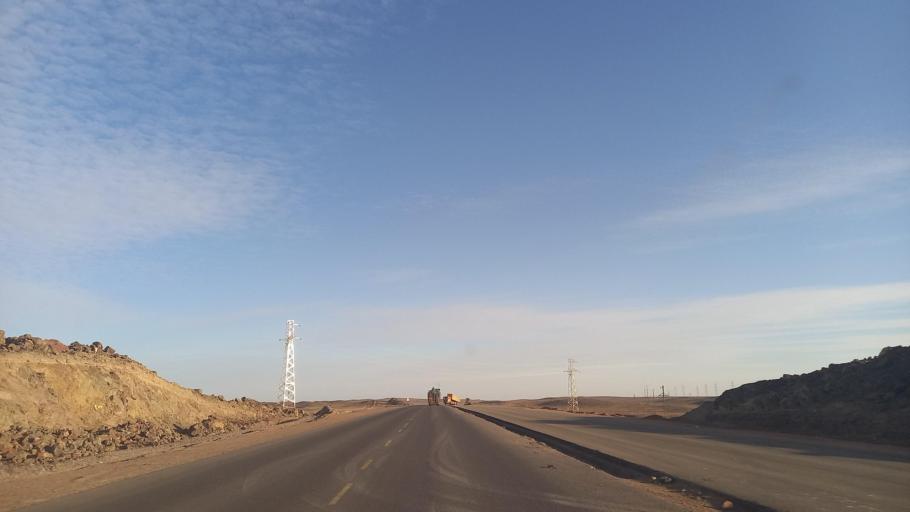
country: KZ
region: Zhambyl
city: Mynaral
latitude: 45.3439
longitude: 73.6990
